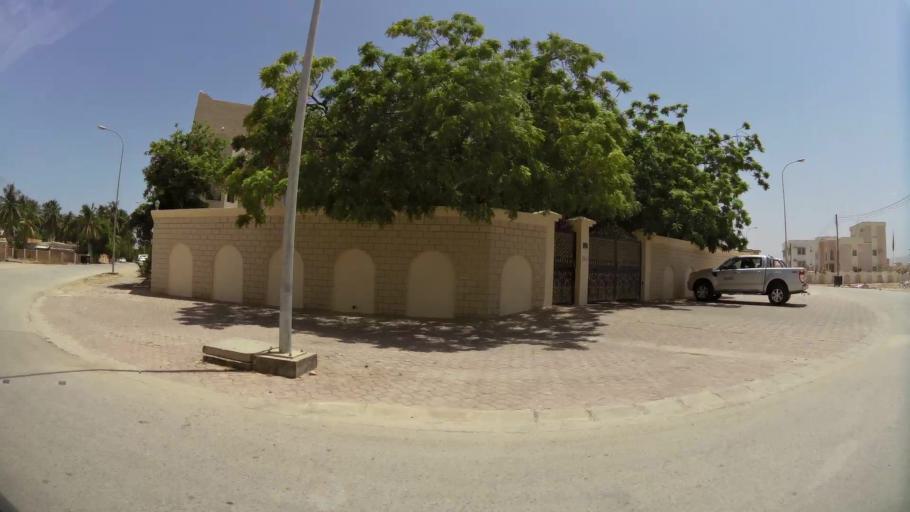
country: OM
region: Zufar
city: Salalah
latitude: 17.0673
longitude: 54.1532
